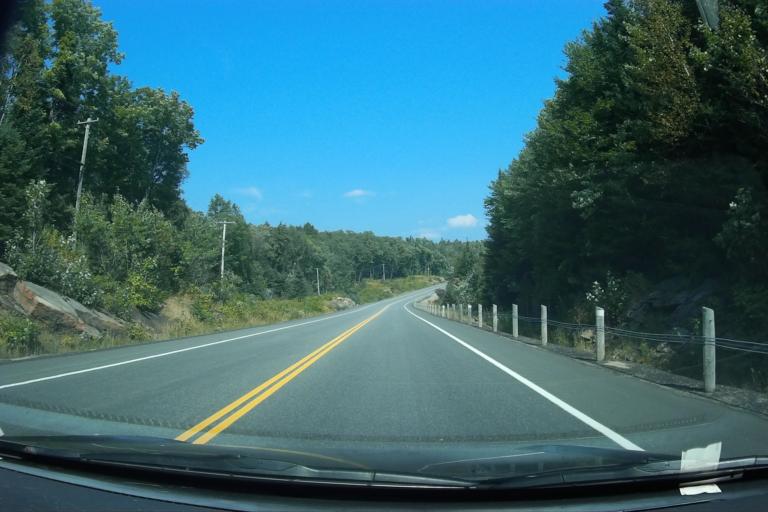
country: CA
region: Ontario
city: Huntsville
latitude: 45.5353
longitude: -78.7027
